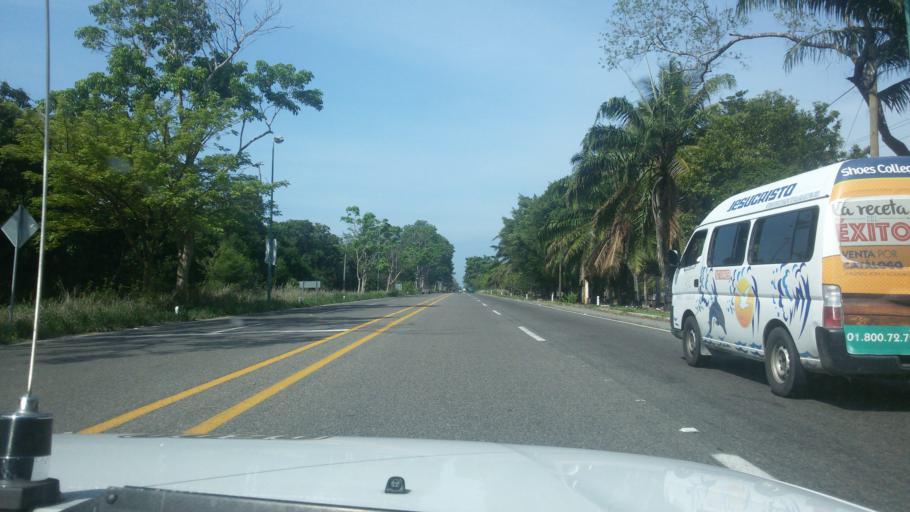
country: MX
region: Chiapas
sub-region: Tapachula
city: Congregacion Reforma
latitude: 14.8091
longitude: -92.3478
